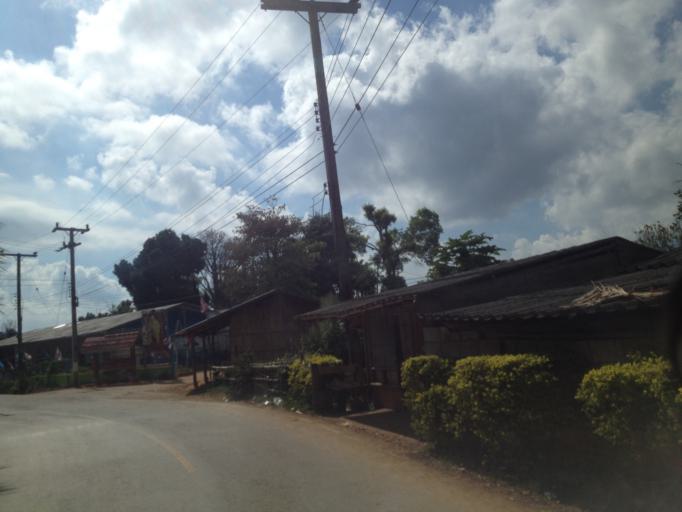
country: TH
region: Mae Hong Son
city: Ban Huai I Huak
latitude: 18.1497
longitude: 98.1313
